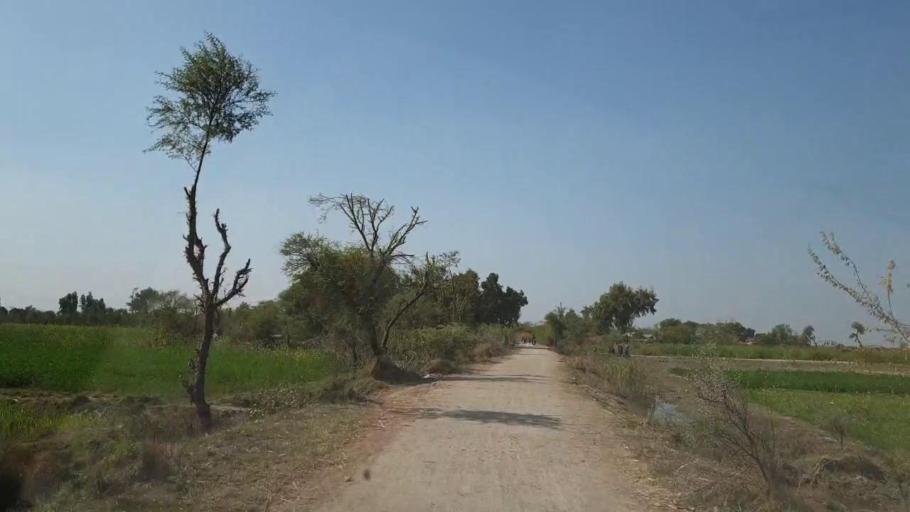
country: PK
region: Sindh
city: Mirpur Khas
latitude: 25.7350
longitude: 69.1083
